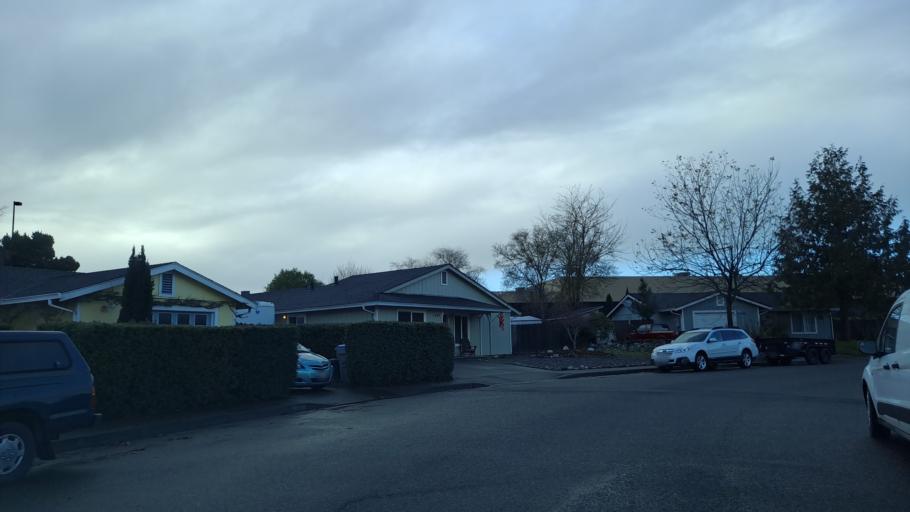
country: US
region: California
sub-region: Humboldt County
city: Fortuna
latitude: 40.5826
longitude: -124.1436
